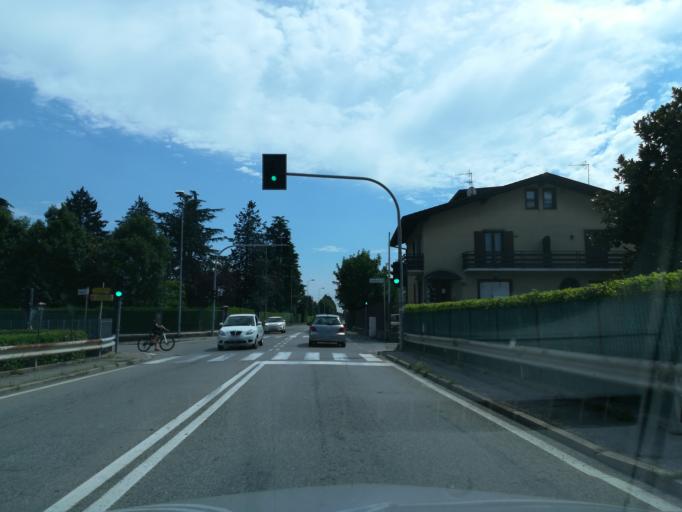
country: IT
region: Lombardy
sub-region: Provincia di Bergamo
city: Almenno San Salvatore
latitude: 45.7474
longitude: 9.6014
